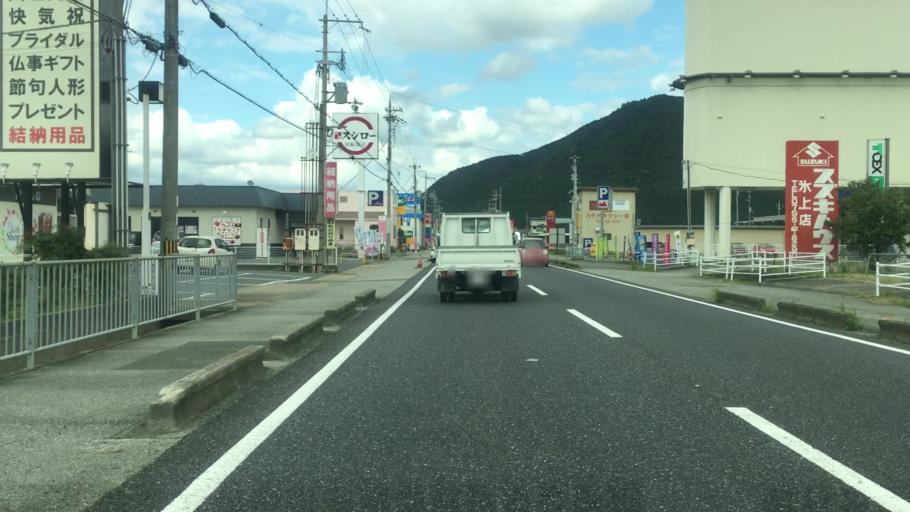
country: JP
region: Kyoto
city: Fukuchiyama
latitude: 35.1558
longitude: 135.0478
